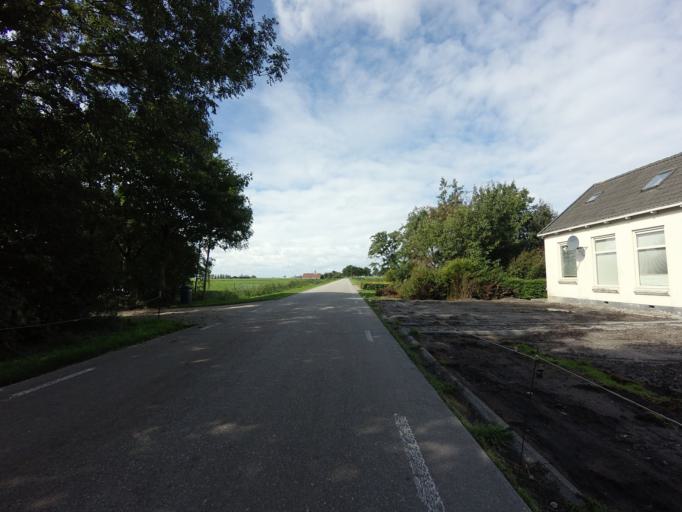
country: NL
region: Friesland
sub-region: Sudwest Fryslan
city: Makkum
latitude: 53.0450
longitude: 5.4390
